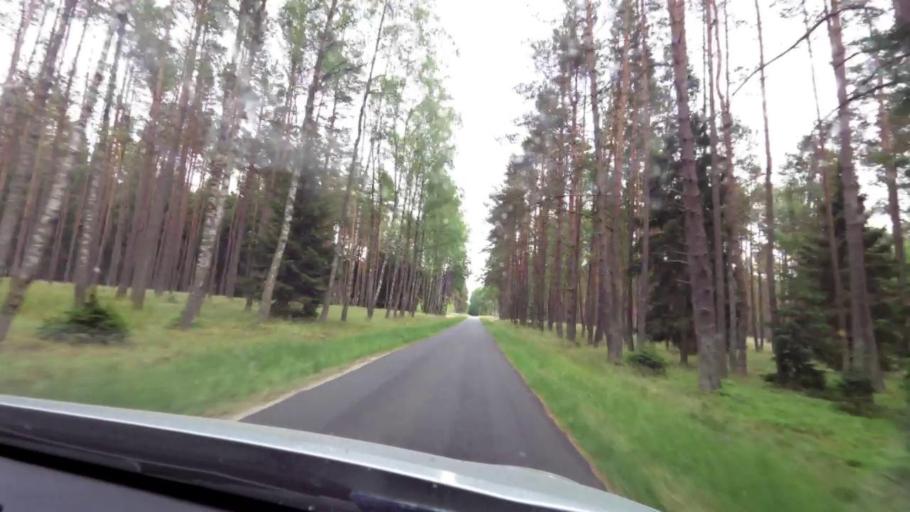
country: PL
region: Pomeranian Voivodeship
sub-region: Powiat bytowski
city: Trzebielino
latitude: 54.1974
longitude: 17.0457
